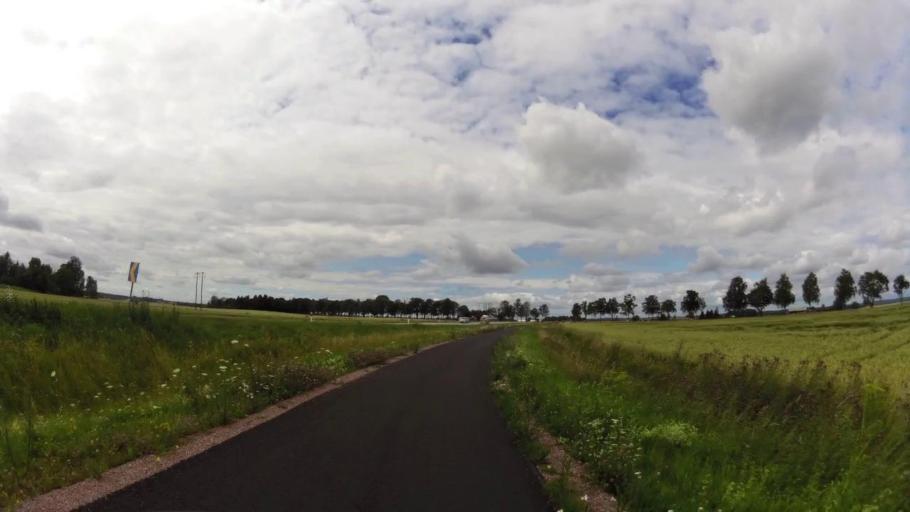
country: SE
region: OEstergoetland
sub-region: Linkopings Kommun
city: Berg
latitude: 58.4451
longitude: 15.5691
